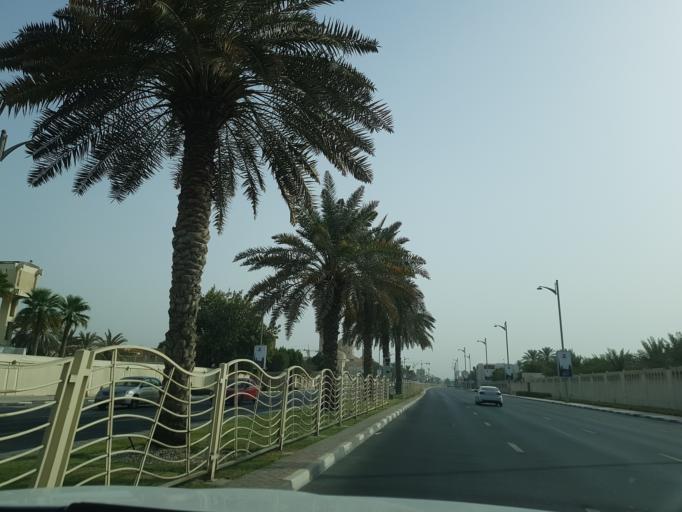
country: AE
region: Ash Shariqah
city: Sharjah
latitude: 25.2367
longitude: 55.2665
